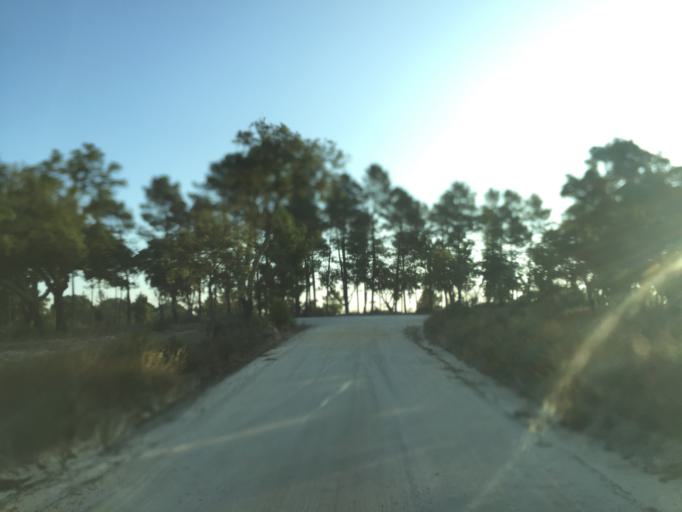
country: PT
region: Portalegre
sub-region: Ponte de Sor
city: Santo Andre
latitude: 39.0919
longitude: -8.3783
